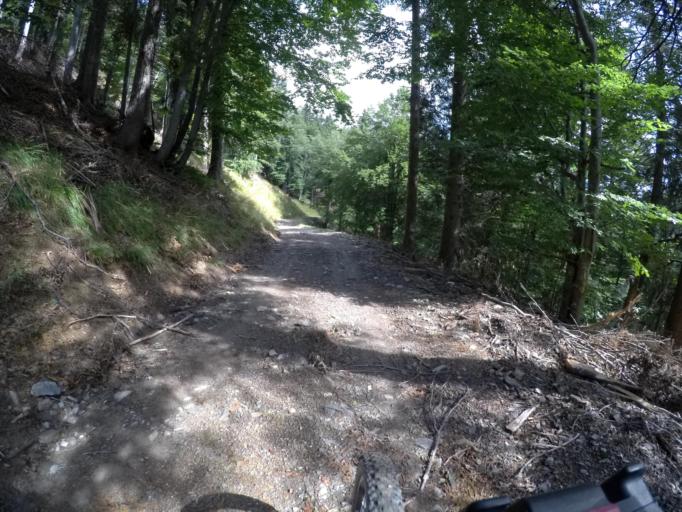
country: IT
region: Friuli Venezia Giulia
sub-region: Provincia di Udine
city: Paularo
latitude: 46.5133
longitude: 13.2064
